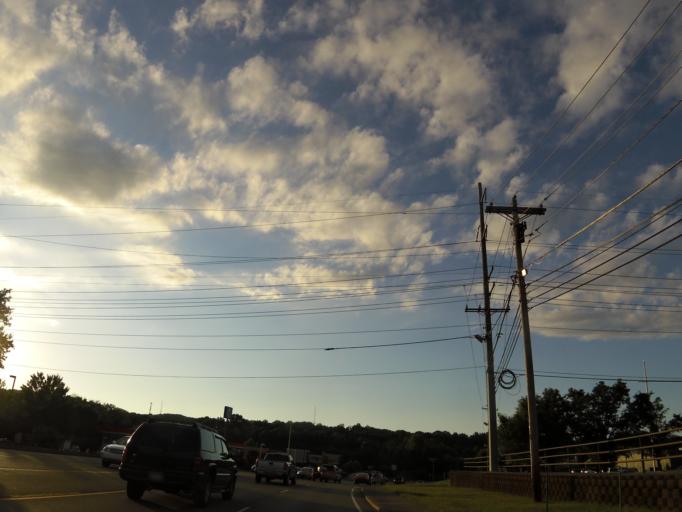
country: US
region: Tennessee
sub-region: Knox County
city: Farragut
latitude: 35.8958
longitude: -84.1748
